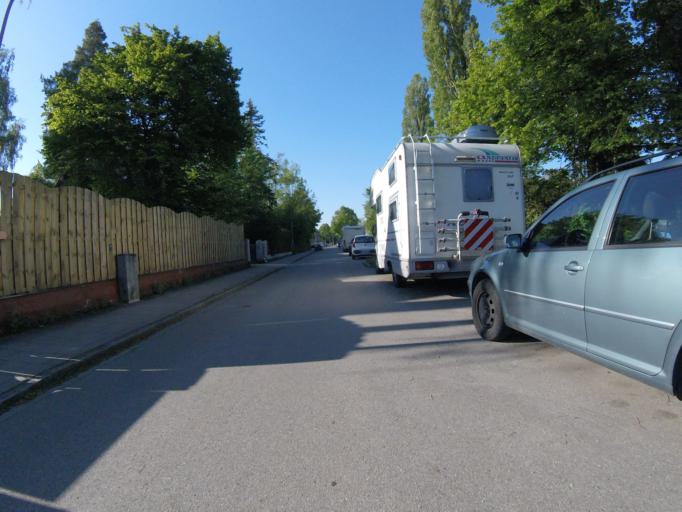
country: DE
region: Bavaria
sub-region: Upper Bavaria
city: Ottobrunn
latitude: 48.0605
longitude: 11.6579
